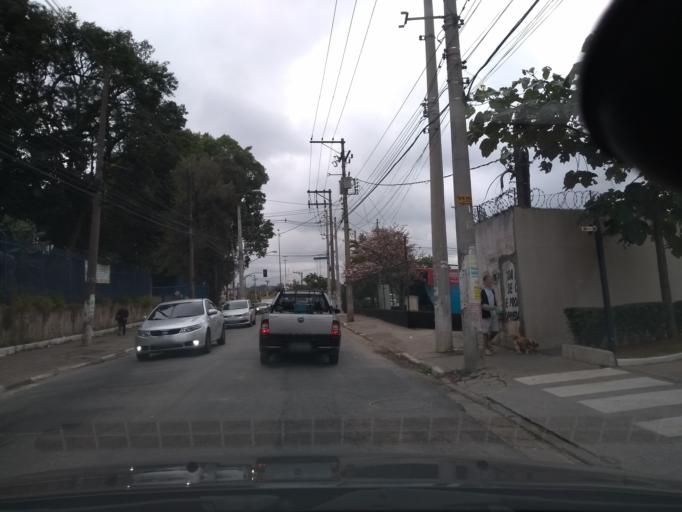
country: BR
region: Sao Paulo
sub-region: Guarulhos
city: Guarulhos
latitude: -23.4618
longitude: -46.4987
